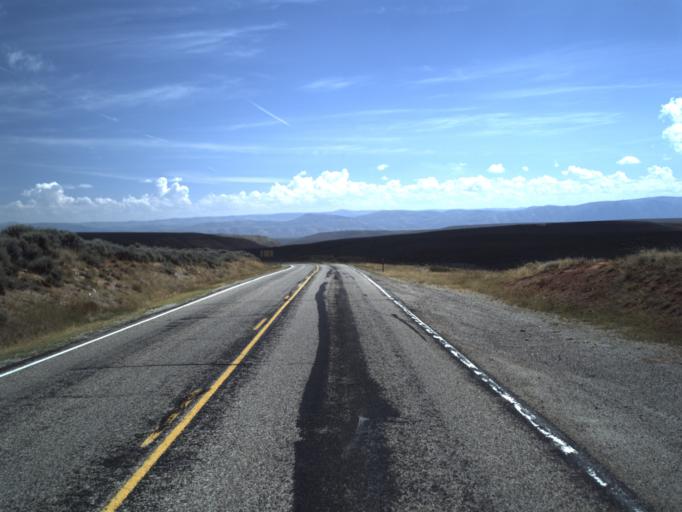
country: US
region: Utah
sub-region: Rich County
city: Randolph
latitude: 41.7963
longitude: -111.2344
